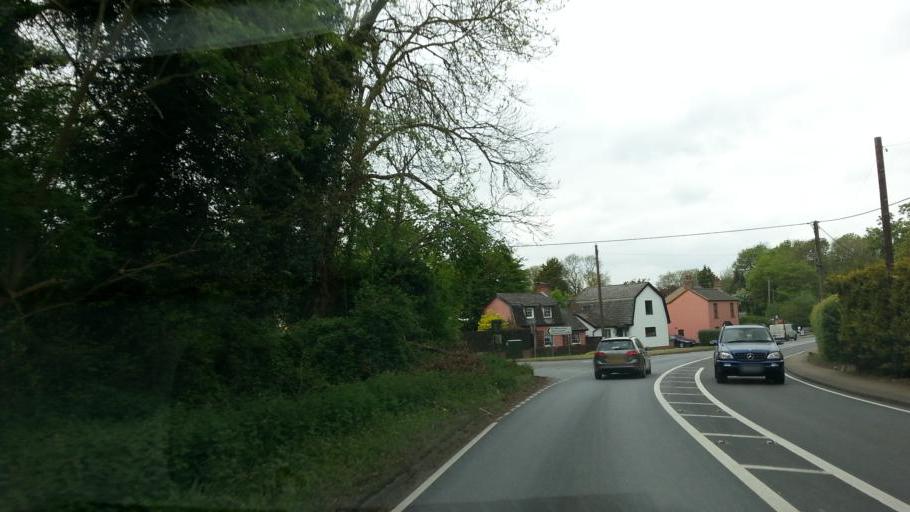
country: GB
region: England
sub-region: Suffolk
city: Bury St Edmunds
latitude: 52.2091
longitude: 0.7491
